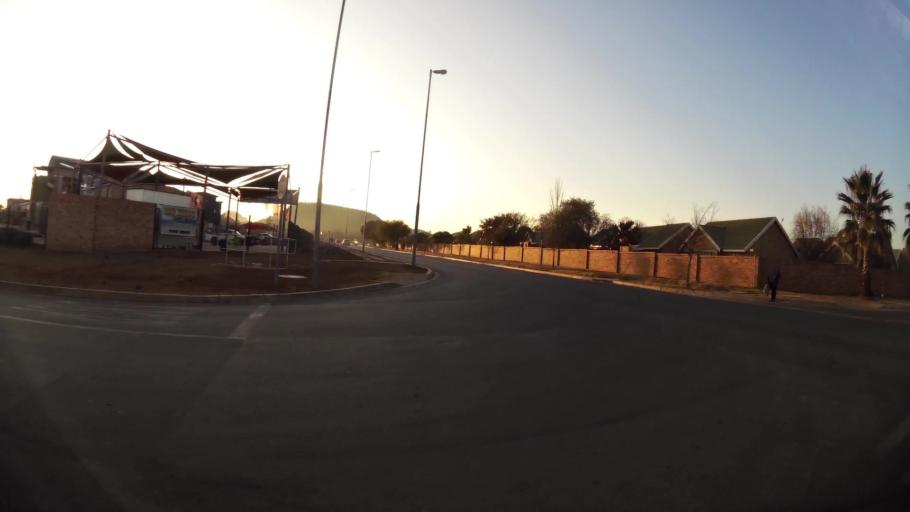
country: ZA
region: Orange Free State
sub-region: Mangaung Metropolitan Municipality
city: Bloemfontein
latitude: -29.0978
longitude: 26.1435
